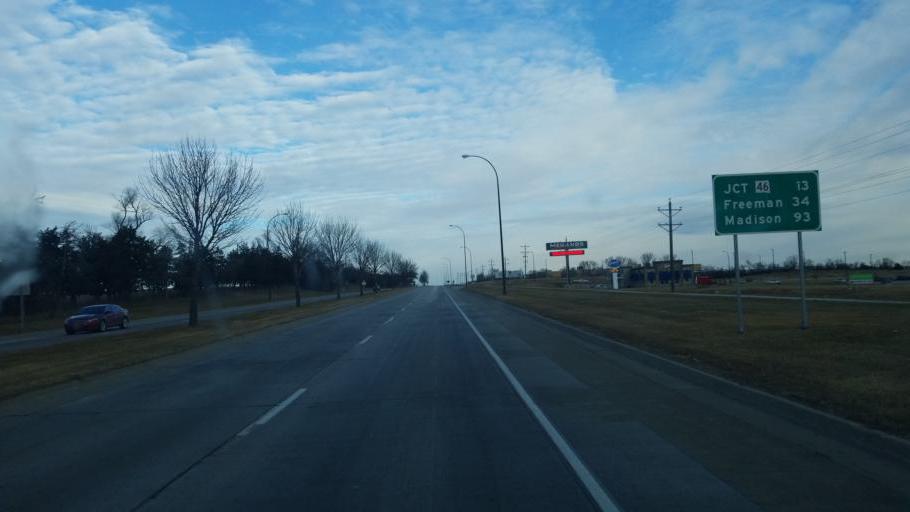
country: US
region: South Dakota
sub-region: Yankton County
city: Yankton
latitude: 42.9102
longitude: -97.3973
